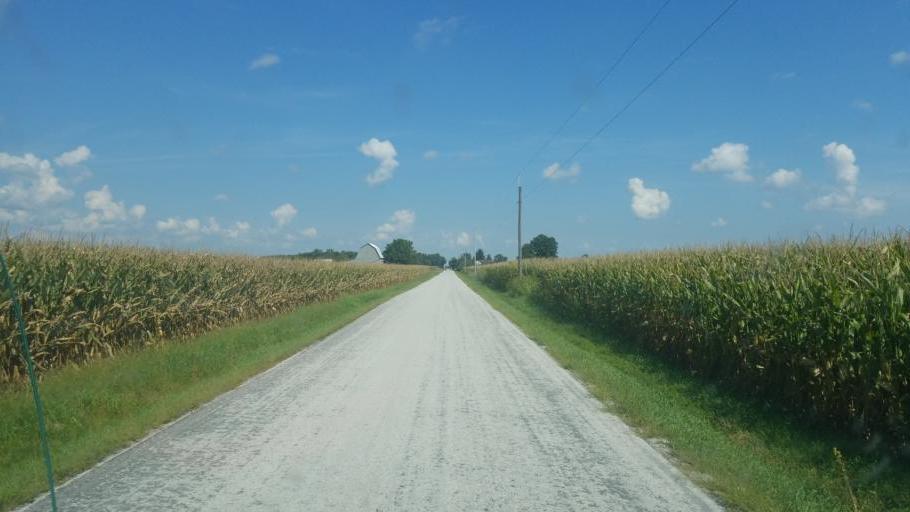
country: US
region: Ohio
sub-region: Hardin County
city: Kenton
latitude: 40.6584
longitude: -83.4958
